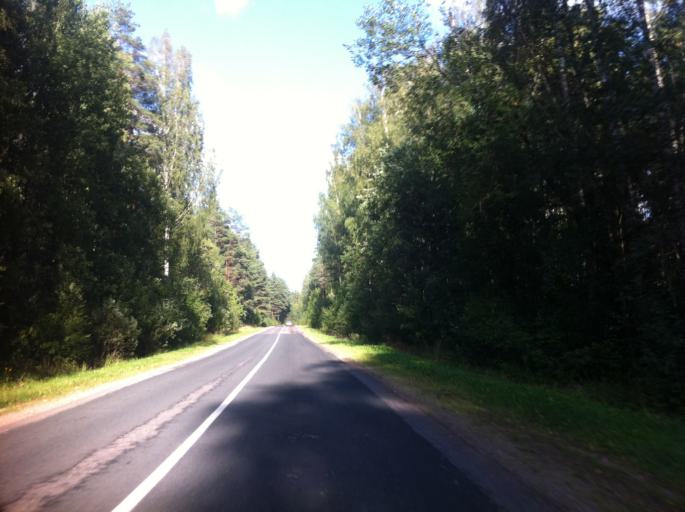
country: RU
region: Pskov
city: Izborsk
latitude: 57.8215
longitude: 27.8525
